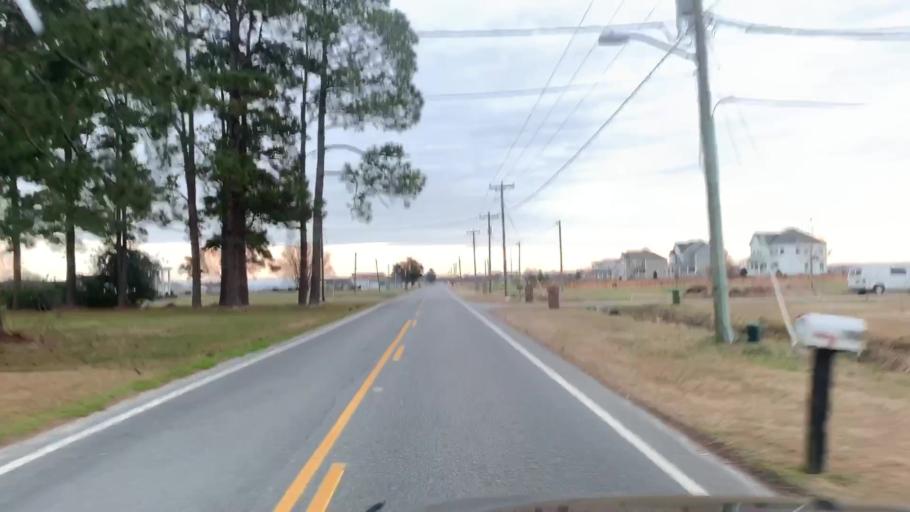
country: US
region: North Carolina
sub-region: Currituck County
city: Moyock
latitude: 36.6237
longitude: -76.1574
